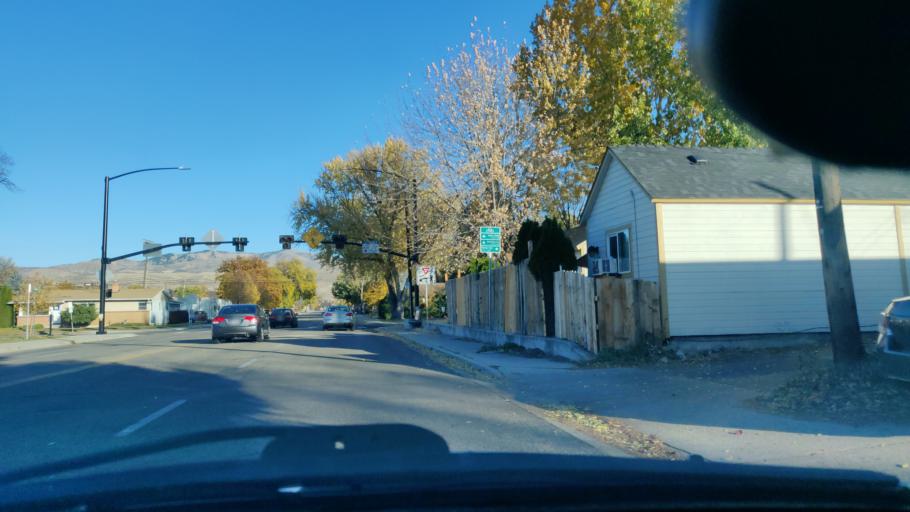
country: US
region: Idaho
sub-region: Ada County
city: Boise
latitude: 43.5984
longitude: -116.1994
